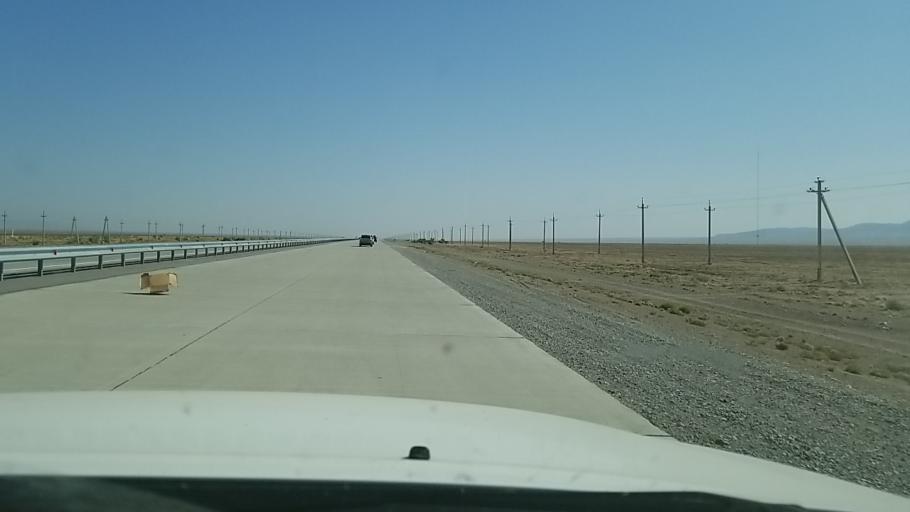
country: KZ
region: Almaty Oblysy
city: Kegen
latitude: 43.7184
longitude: 78.7364
